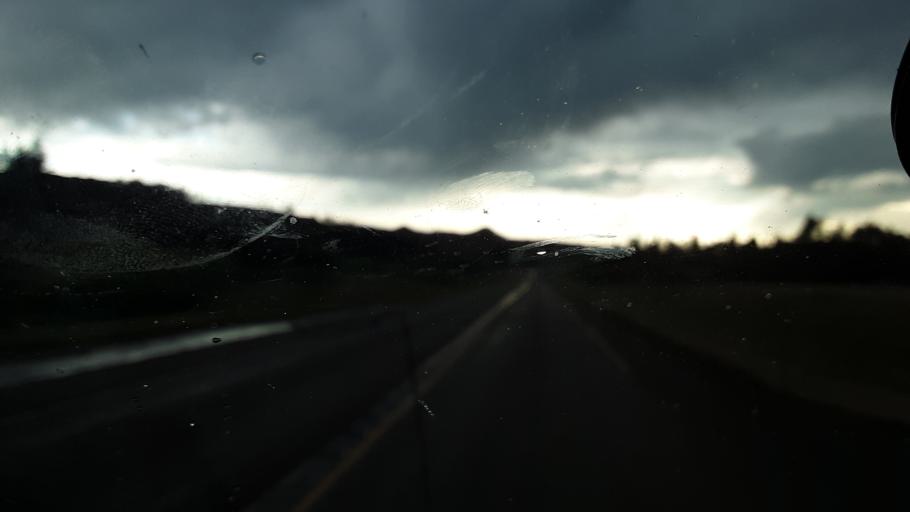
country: US
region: Montana
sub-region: Powder River County
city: Broadus
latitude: 45.5512
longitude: -105.9231
